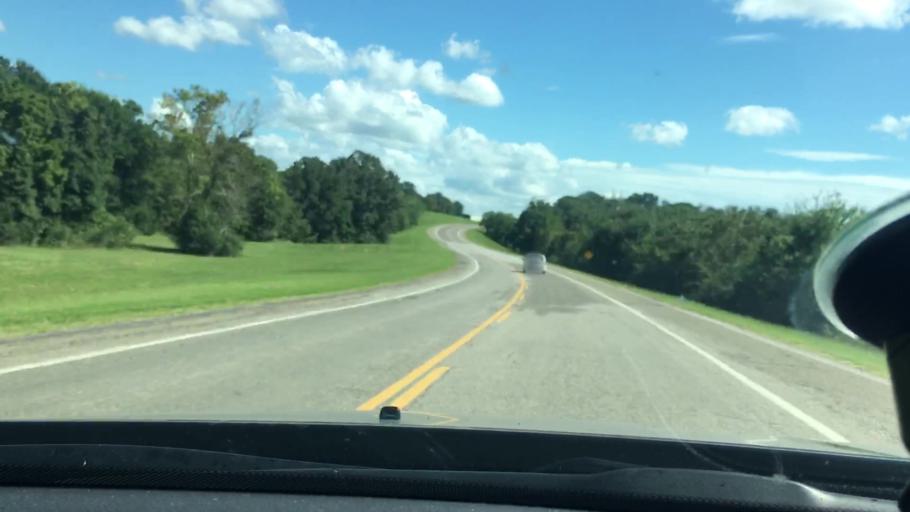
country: US
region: Oklahoma
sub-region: Sequoyah County
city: Vian
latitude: 35.5177
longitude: -94.9727
